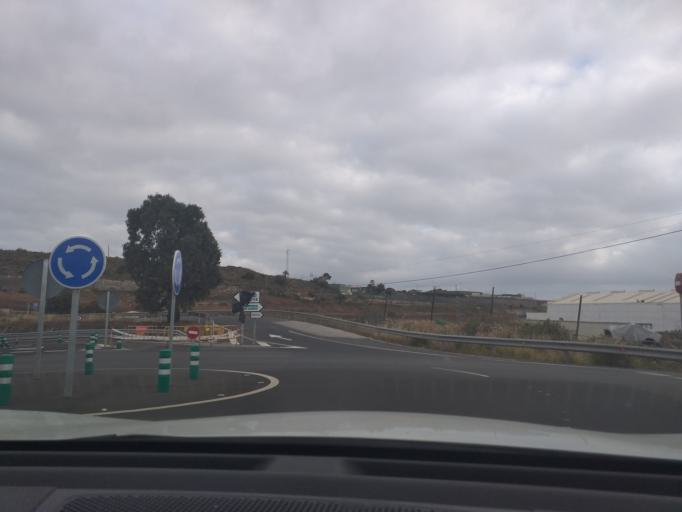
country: ES
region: Canary Islands
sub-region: Provincia de Las Palmas
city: Arucas
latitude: 28.1085
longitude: -15.4892
